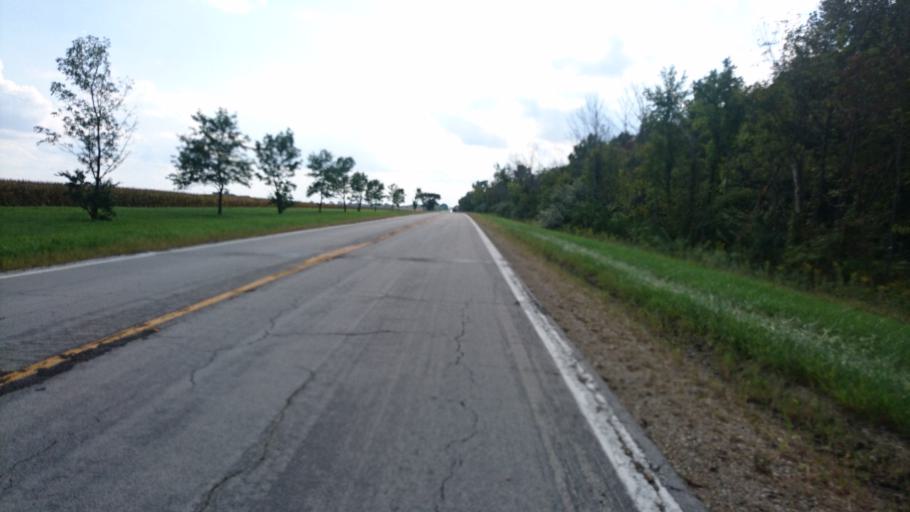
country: US
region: Illinois
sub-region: McLean County
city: Twin Grove
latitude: 40.3556
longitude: -89.1213
